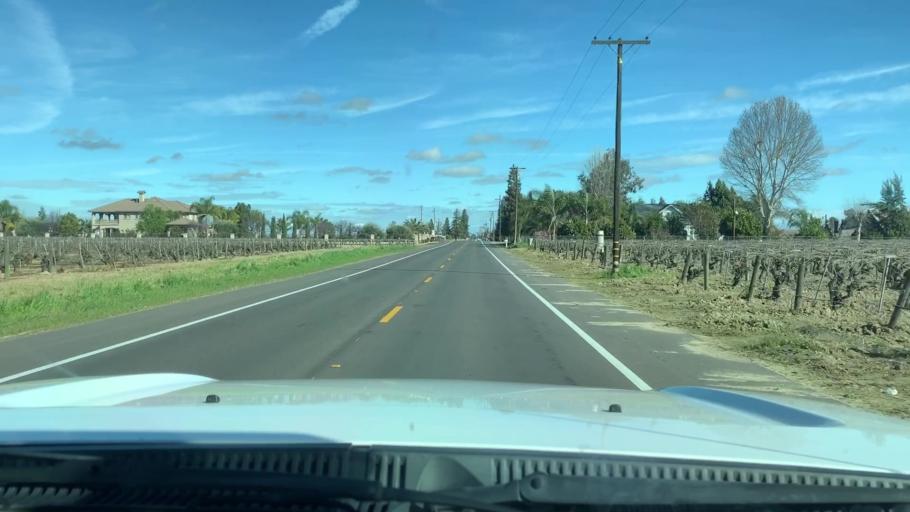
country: US
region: California
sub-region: Fresno County
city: Fowler
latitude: 36.5643
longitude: -119.6824
